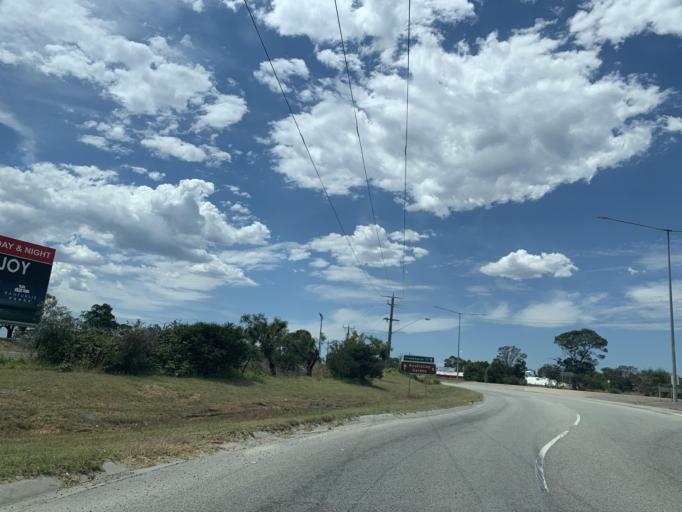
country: AU
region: Victoria
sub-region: Casey
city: Cranbourne South
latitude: -38.1240
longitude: 145.2488
